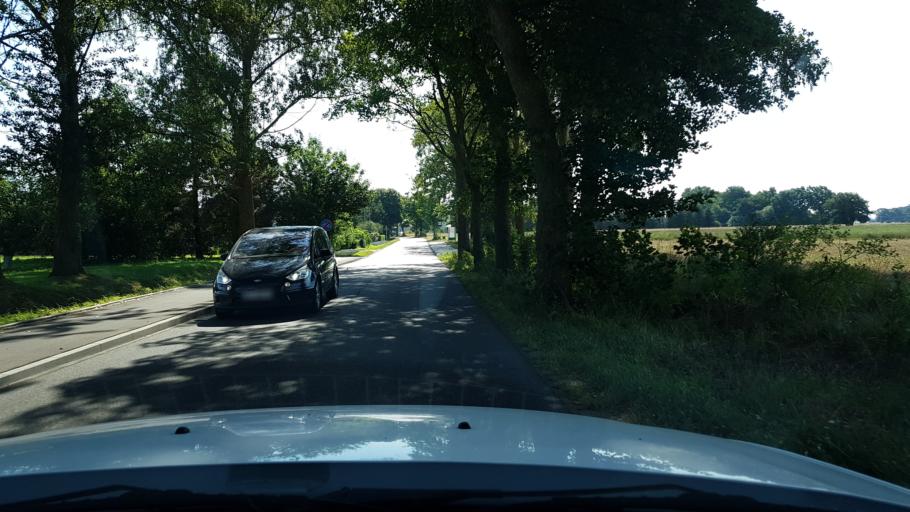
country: PL
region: West Pomeranian Voivodeship
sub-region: Powiat koszalinski
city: Sianow
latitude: 54.2736
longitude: 16.2302
